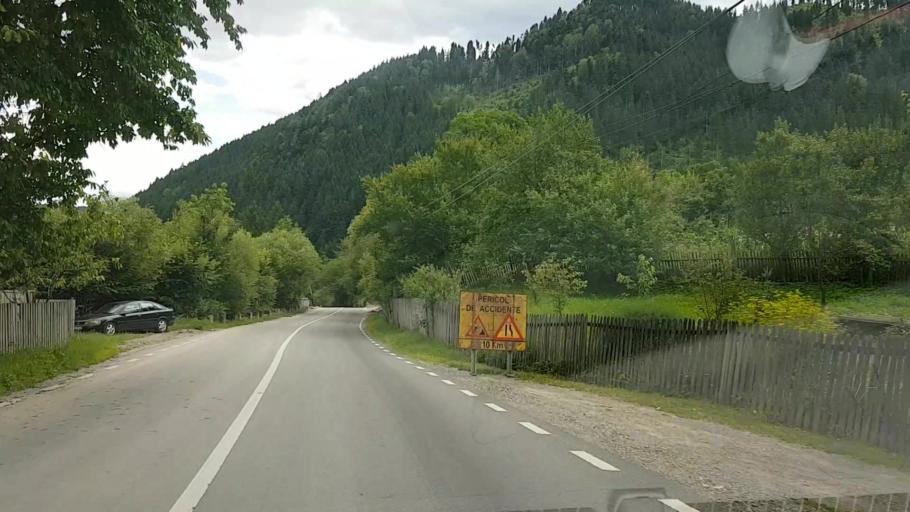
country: RO
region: Neamt
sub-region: Comuna Poiana Teiului
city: Poiana Teiului
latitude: 47.0957
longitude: 25.9428
